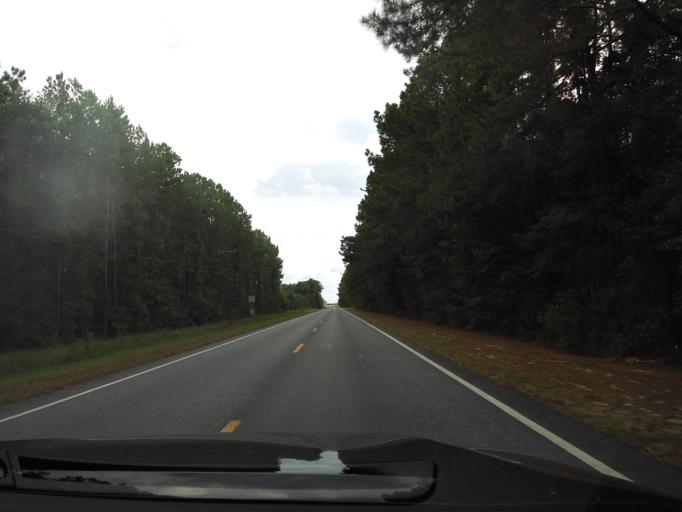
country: US
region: Georgia
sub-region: Liberty County
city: Midway
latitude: 31.6692
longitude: -81.4008
